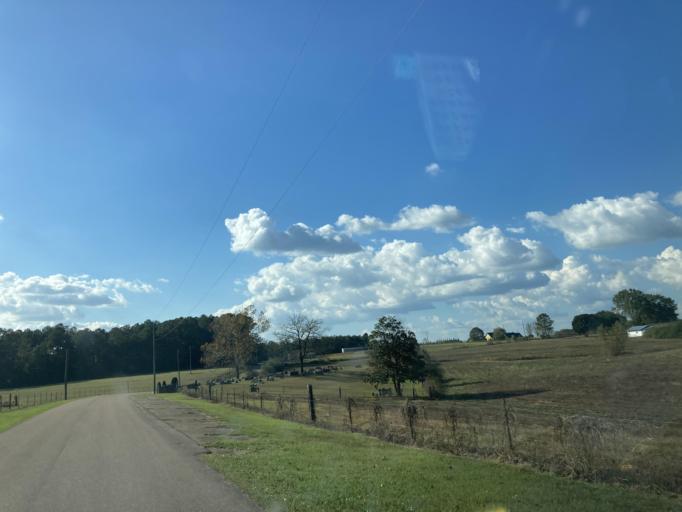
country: US
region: Mississippi
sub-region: Lamar County
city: Sumrall
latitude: 31.4210
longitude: -89.6384
